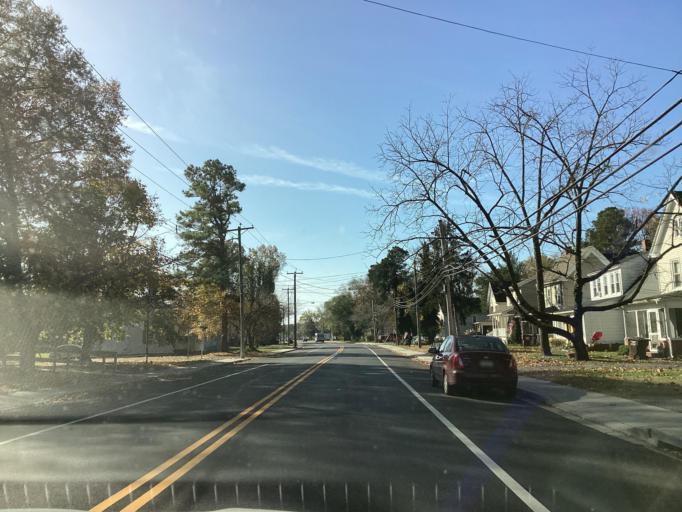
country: US
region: Maryland
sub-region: Dorchester County
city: Cambridge
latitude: 38.5579
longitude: -76.0805
